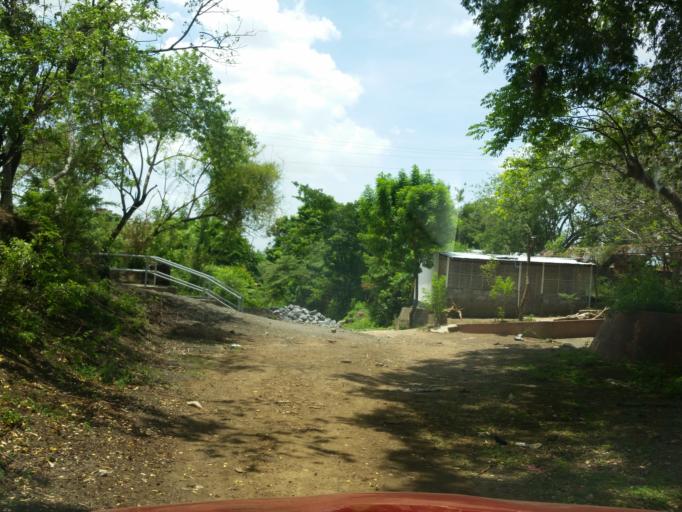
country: NI
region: Managua
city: Managua
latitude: 12.1020
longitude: -86.2730
